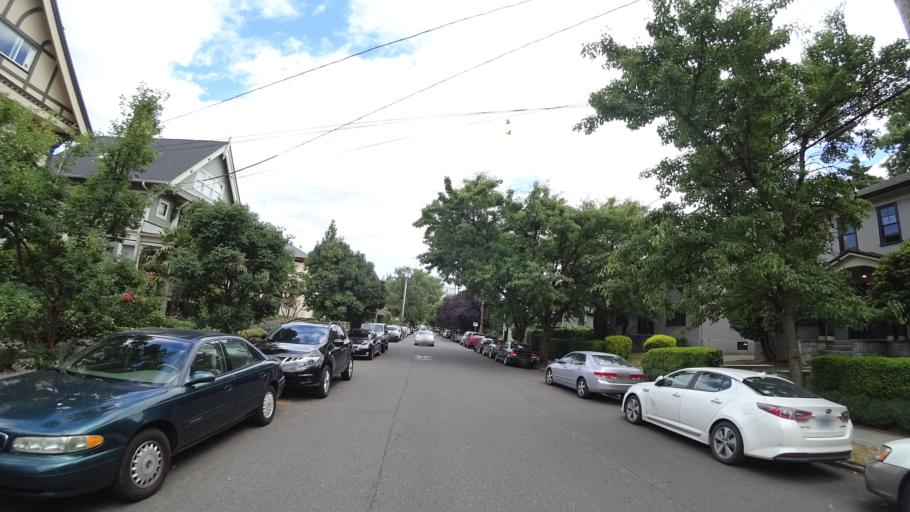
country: US
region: Oregon
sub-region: Multnomah County
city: Portland
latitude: 45.5320
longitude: -122.6941
